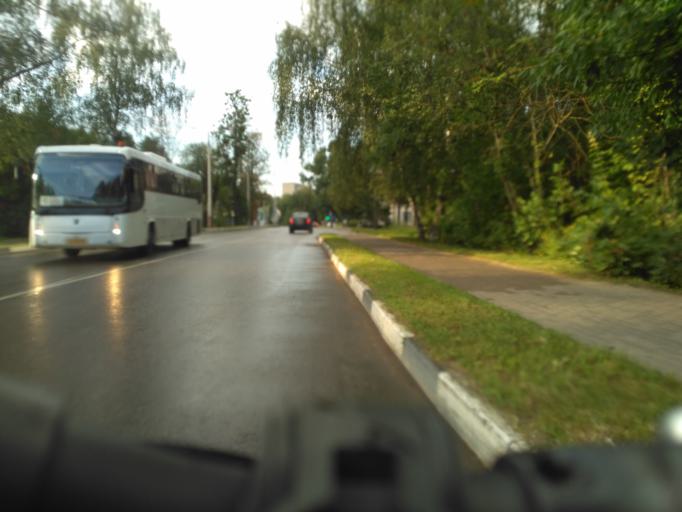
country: RU
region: Moskovskaya
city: Dubna
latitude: 56.7420
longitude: 37.1779
